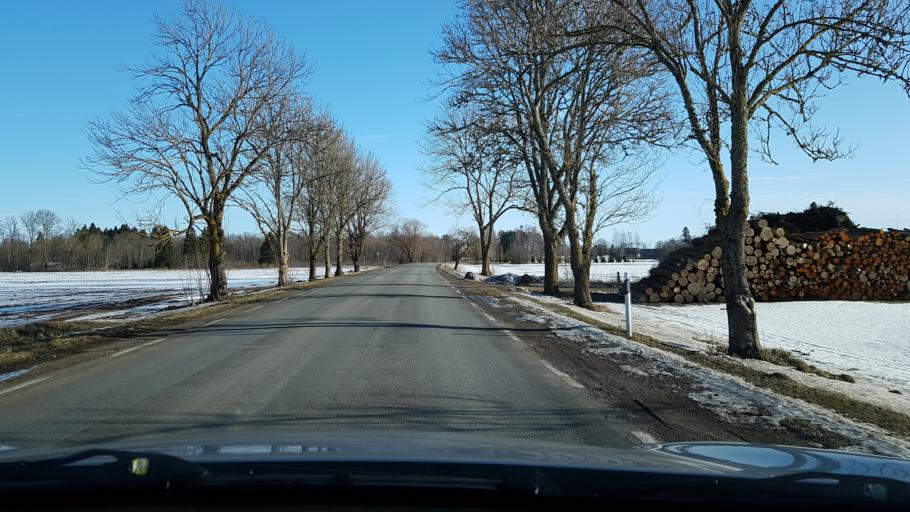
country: EE
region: Viljandimaa
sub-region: Vohma linn
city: Vohma
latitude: 58.6314
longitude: 25.5795
